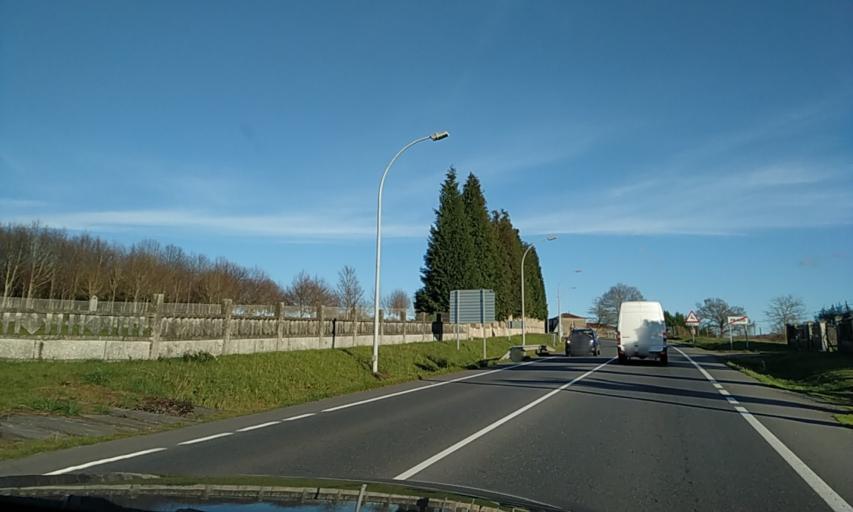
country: ES
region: Galicia
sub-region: Provincia de Pontevedra
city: Silleda
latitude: 42.6819
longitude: -8.1794
